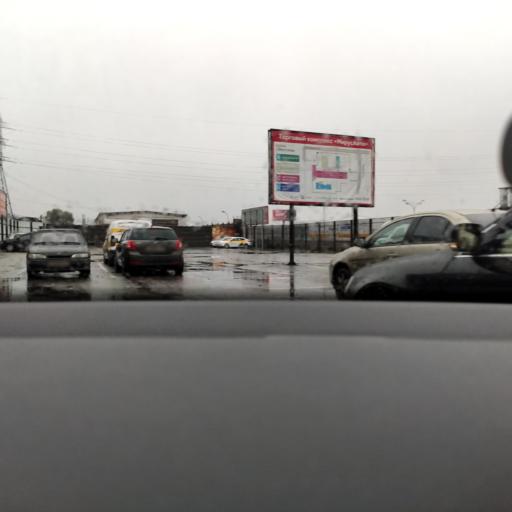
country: RU
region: Moskovskaya
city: Nemchinovka
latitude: 55.7263
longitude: 37.3808
